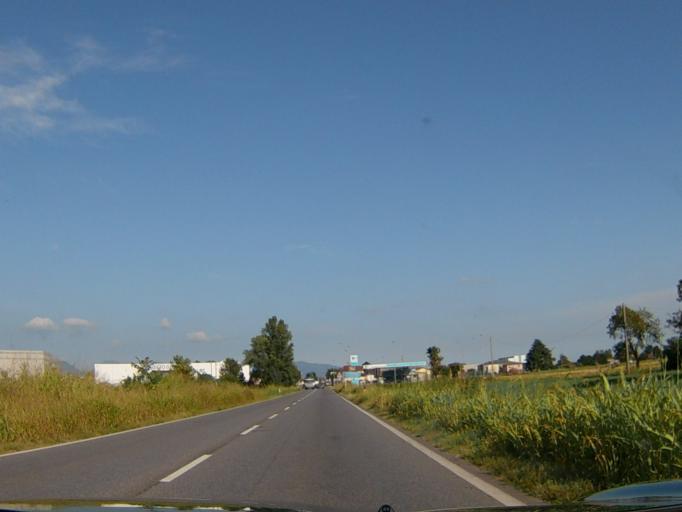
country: IT
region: Lombardy
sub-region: Provincia di Brescia
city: Lodetto
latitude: 45.5584
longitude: 10.0366
